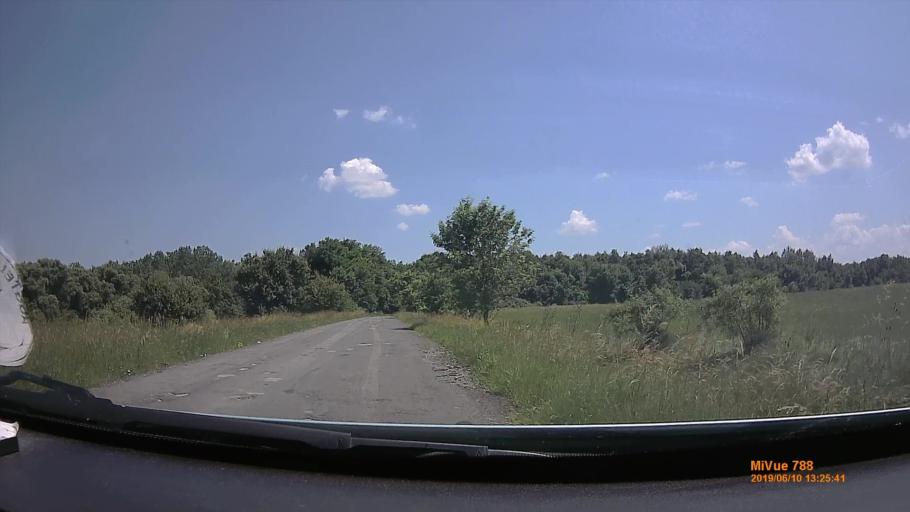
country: HU
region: Borsod-Abauj-Zemplen
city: Tiszaluc
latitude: 48.0154
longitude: 21.1124
